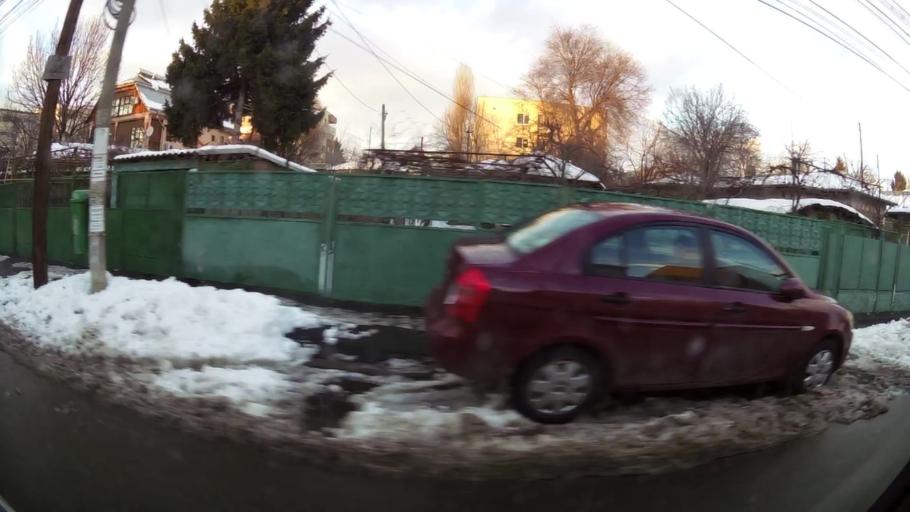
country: RO
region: Ilfov
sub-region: Comuna Popesti-Leordeni
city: Popesti-Leordeni
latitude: 44.3795
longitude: 26.1395
